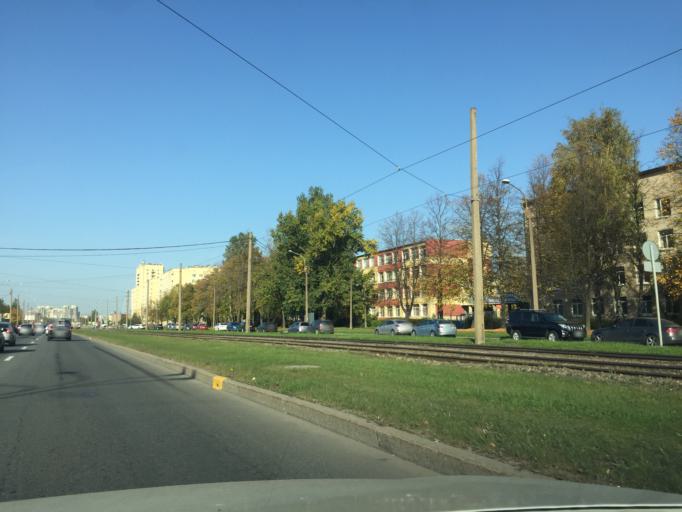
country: RU
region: St.-Petersburg
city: Grazhdanka
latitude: 60.0094
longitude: 30.4349
